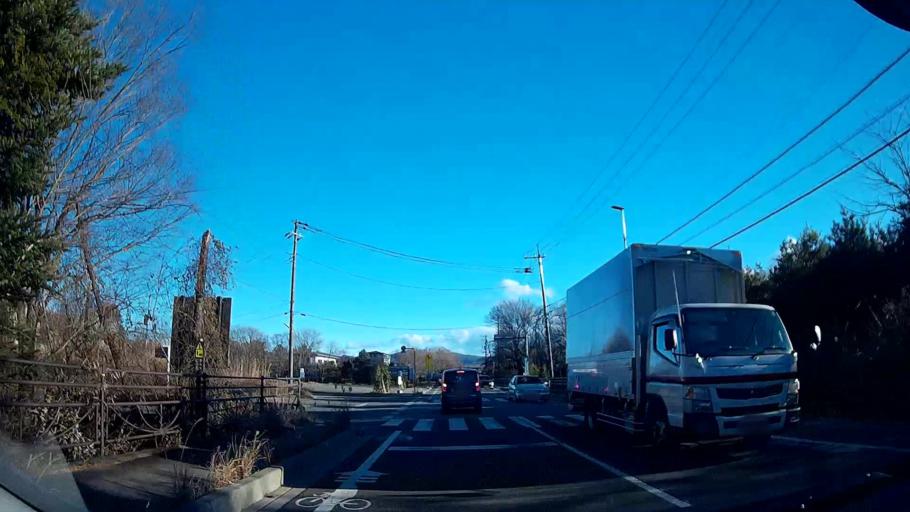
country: JP
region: Shizuoka
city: Gotemba
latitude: 35.4334
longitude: 138.8422
